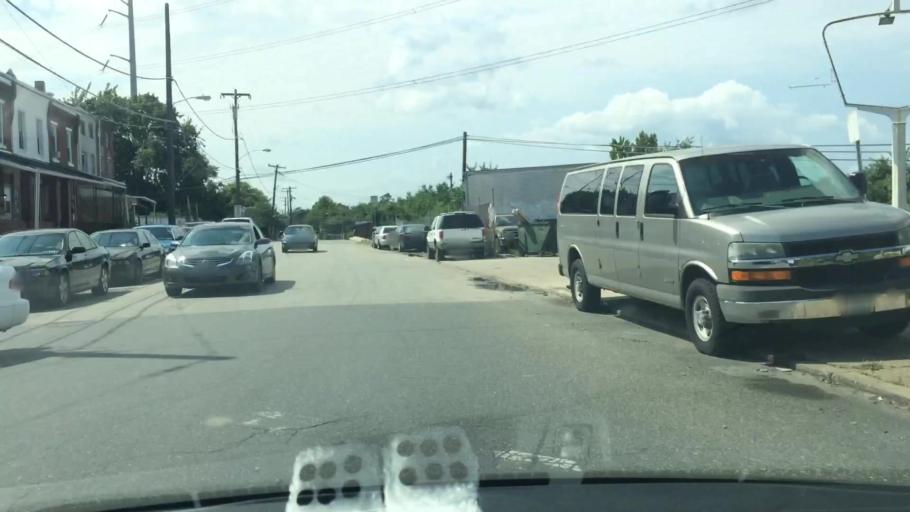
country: US
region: Pennsylvania
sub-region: Delaware County
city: Yeadon
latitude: 39.9285
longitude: -75.2330
